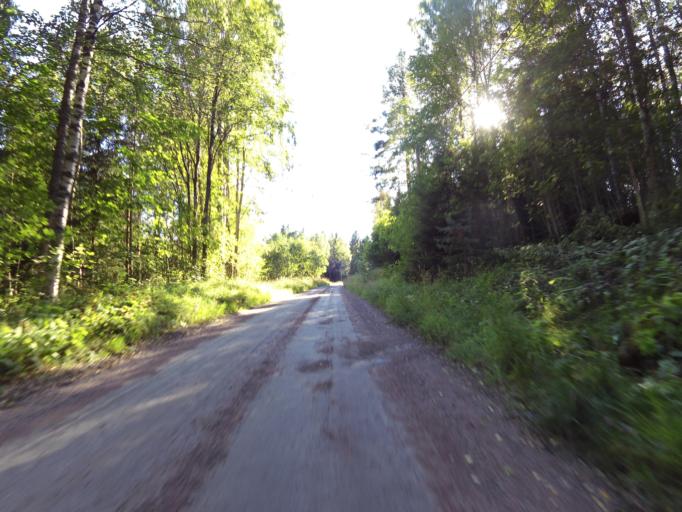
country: SE
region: Gaevleborg
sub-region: Hofors Kommun
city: Hofors
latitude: 60.5689
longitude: 16.2594
